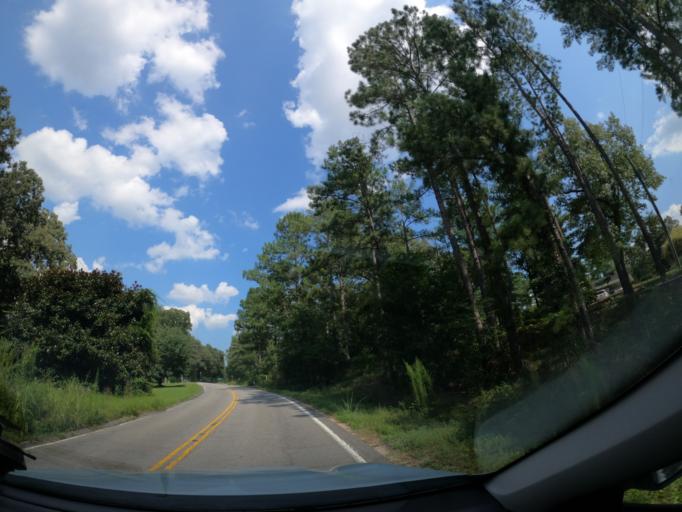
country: US
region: South Carolina
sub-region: Lexington County
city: South Congaree
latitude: 33.9068
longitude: -81.1625
